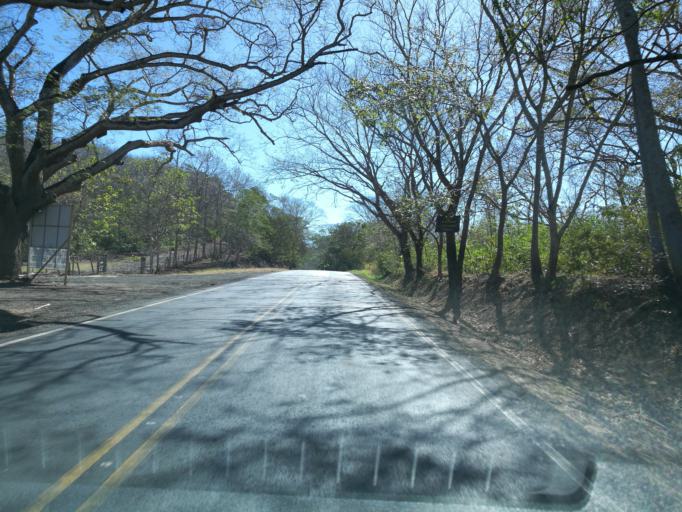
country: CR
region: Puntarenas
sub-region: Canton Central de Puntarenas
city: Puntarenas
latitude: 10.0876
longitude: -84.8434
